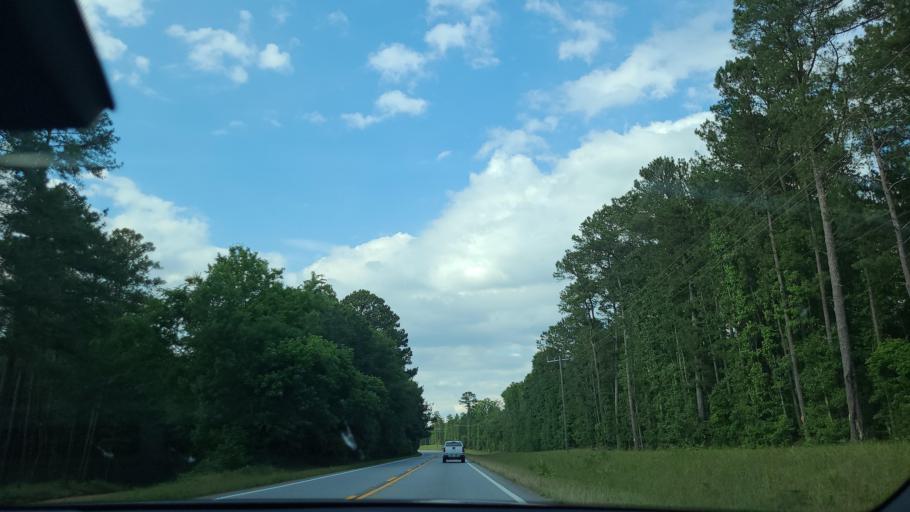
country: US
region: Georgia
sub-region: Jones County
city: Gray
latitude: 33.1099
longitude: -83.4817
